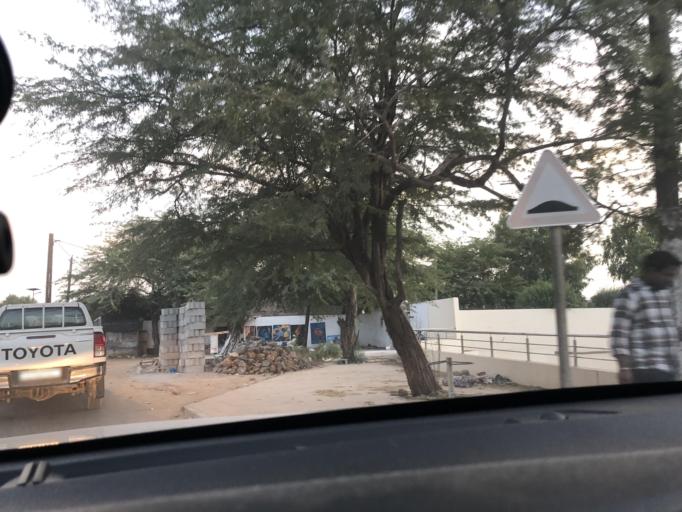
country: SN
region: Dakar
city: Mermoz Boabab
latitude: 14.7375
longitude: -17.5138
